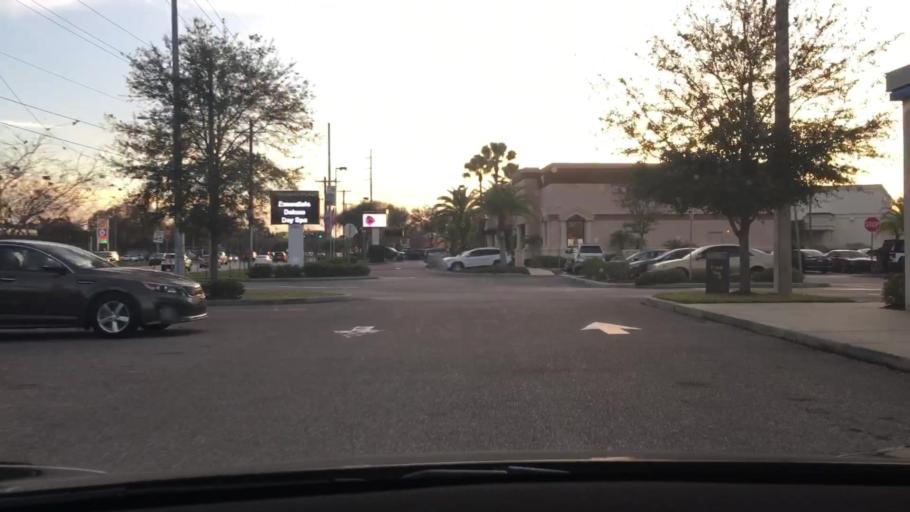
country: US
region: Florida
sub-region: Hillsborough County
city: Greater Northdale
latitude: 28.0844
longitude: -82.5404
